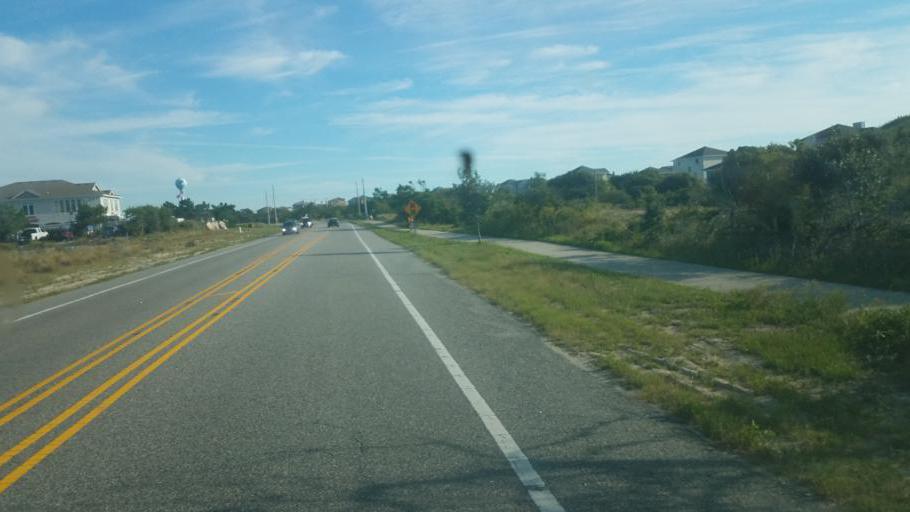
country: US
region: North Carolina
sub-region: Dare County
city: Southern Shores
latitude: 36.3002
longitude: -75.8042
